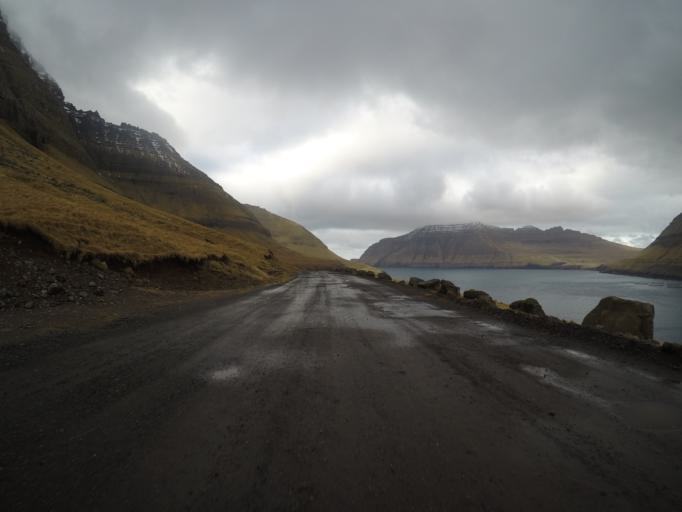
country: FO
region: Nordoyar
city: Klaksvik
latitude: 62.3371
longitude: -6.5787
